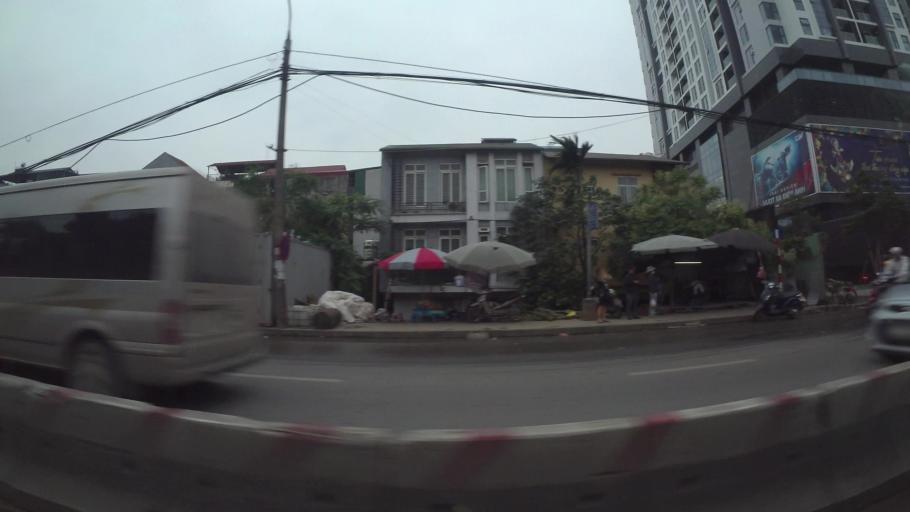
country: VN
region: Ha Noi
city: Hai BaTrung
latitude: 21.0103
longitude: 105.8646
